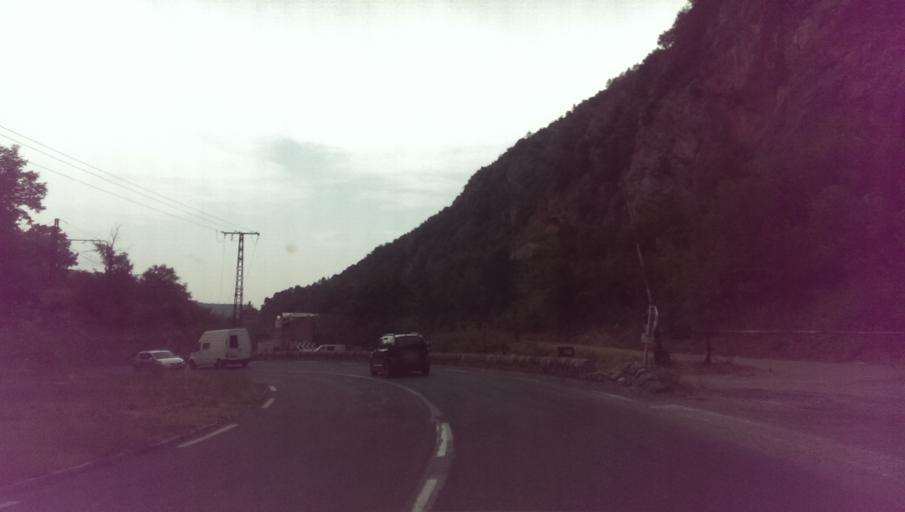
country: FR
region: Languedoc-Roussillon
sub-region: Departement des Pyrenees-Orientales
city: Ria-Sirach
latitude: 42.5957
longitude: 2.3761
